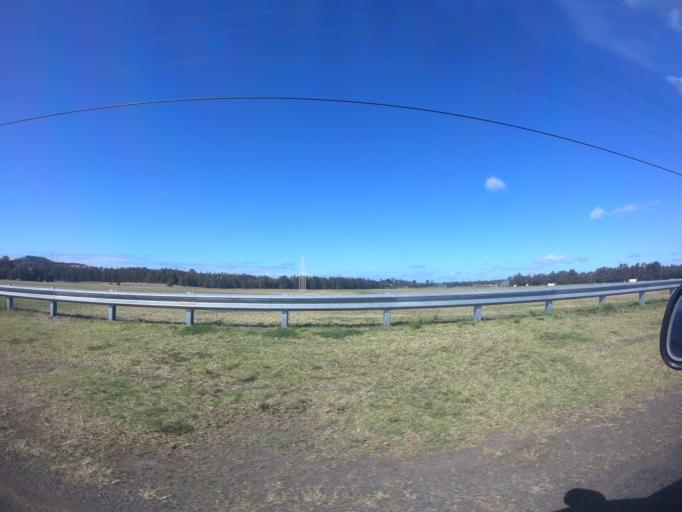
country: AU
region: New South Wales
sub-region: Wollongong
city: Berkeley
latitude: -34.4817
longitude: 150.8332
